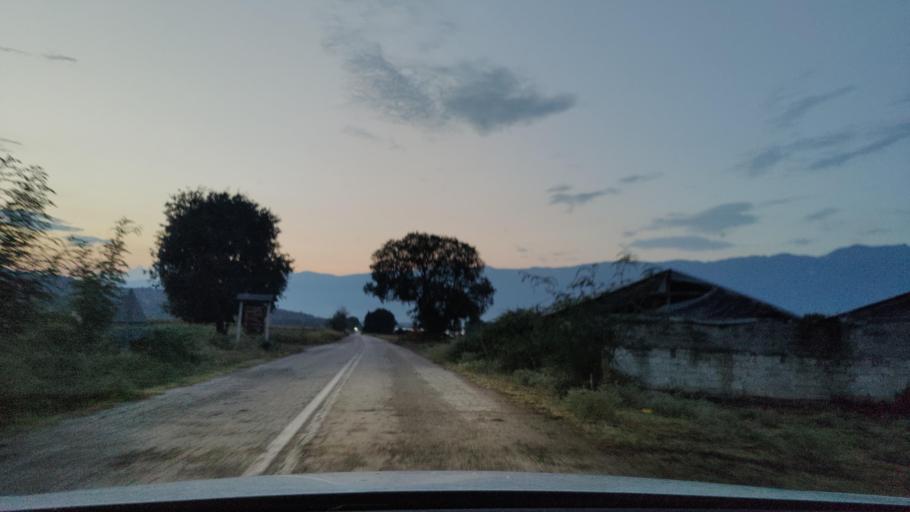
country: GR
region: Central Macedonia
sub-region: Nomos Serron
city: Chrysochorafa
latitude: 41.1828
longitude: 23.1056
